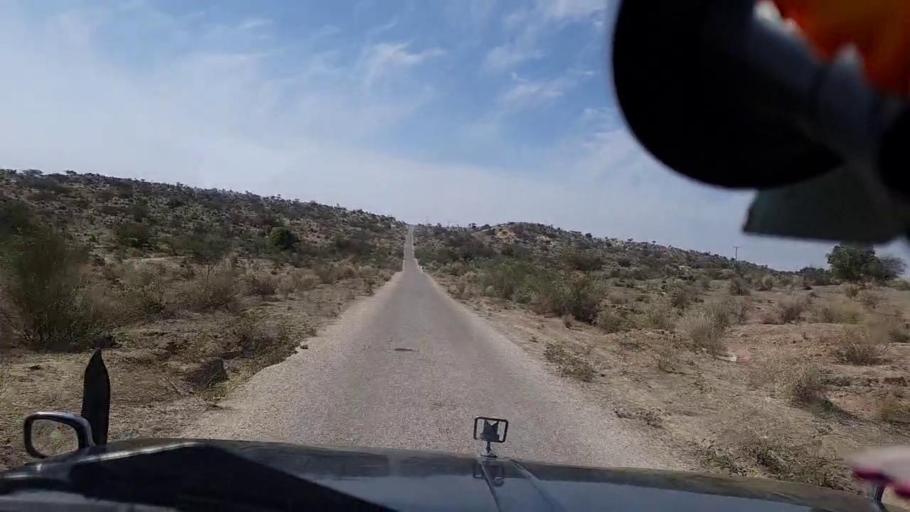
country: PK
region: Sindh
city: Diplo
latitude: 24.3882
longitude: 69.5882
